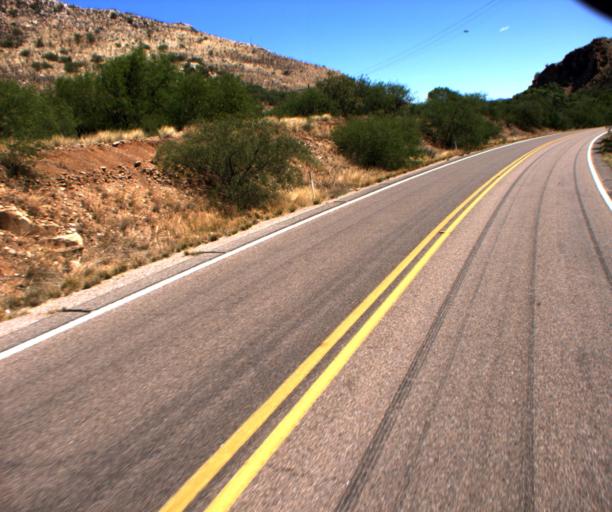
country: US
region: Arizona
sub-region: Santa Cruz County
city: Rio Rico
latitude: 31.5055
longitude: -110.8071
